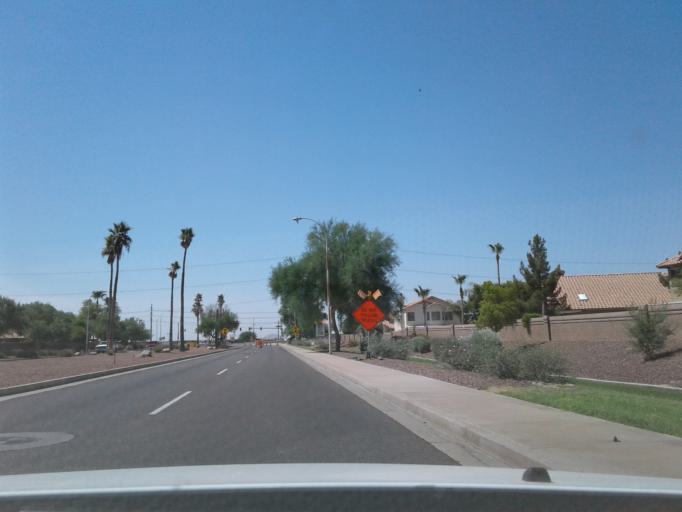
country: US
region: Arizona
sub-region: Maricopa County
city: Guadalupe
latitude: 33.2936
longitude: -112.0147
